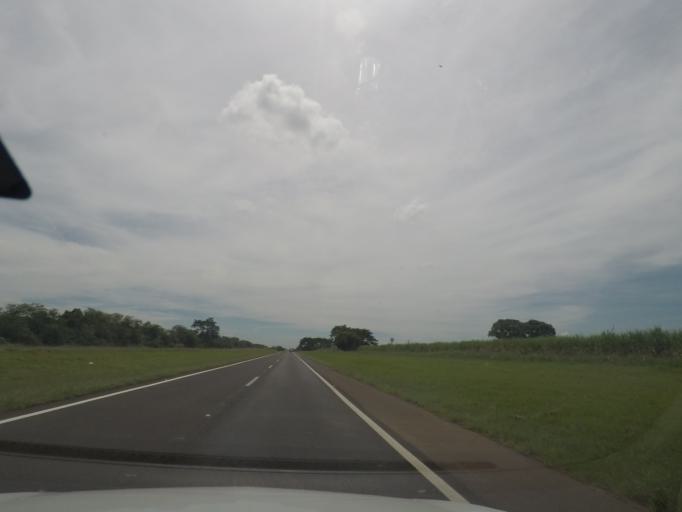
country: BR
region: Sao Paulo
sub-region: Bebedouro
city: Bebedouro
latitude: -20.9853
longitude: -48.4353
